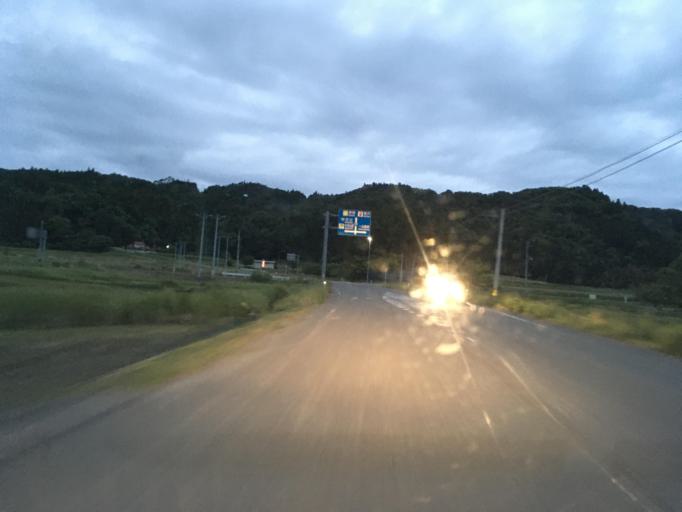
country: JP
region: Miyagi
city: Furukawa
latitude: 38.7699
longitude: 140.8881
